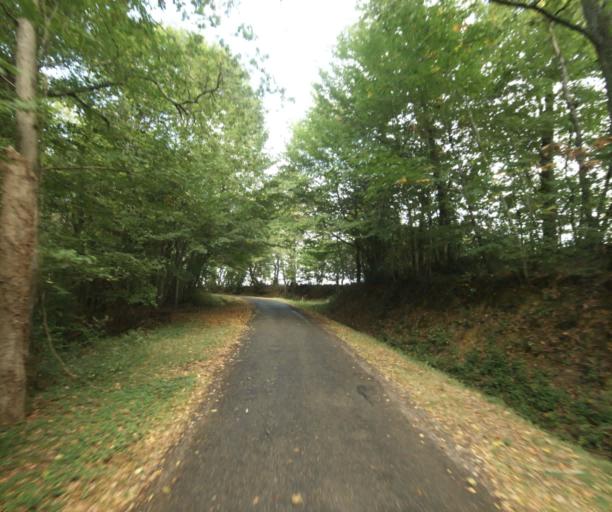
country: FR
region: Aquitaine
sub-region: Departement des Landes
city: Villeneuve-de-Marsan
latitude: 43.9105
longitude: -0.2175
